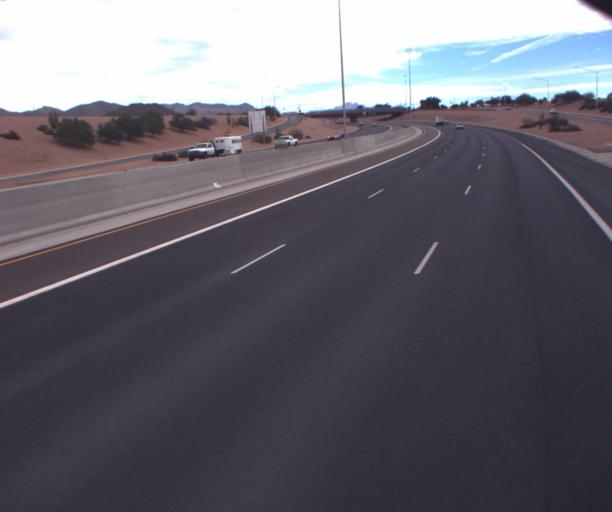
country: US
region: Arizona
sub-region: Maricopa County
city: Mesa
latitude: 33.4762
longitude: -111.7069
